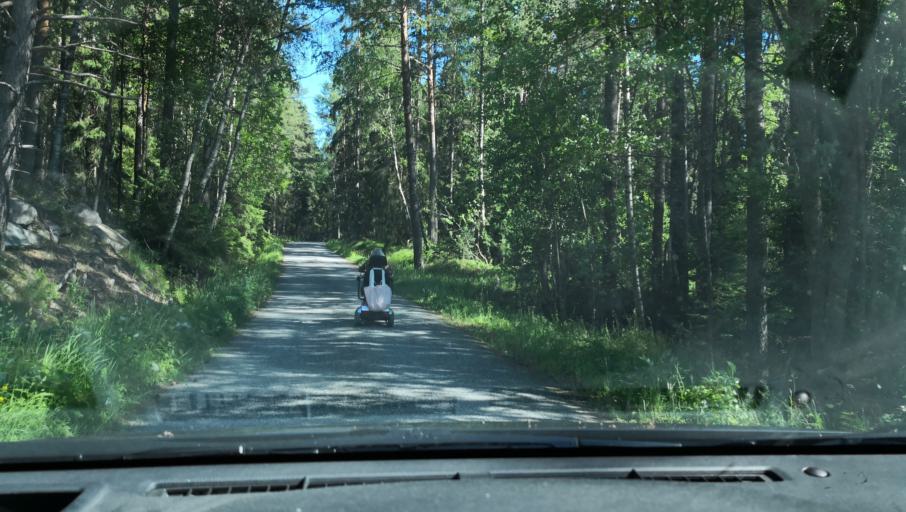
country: SE
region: Soedermanland
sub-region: Eskilstuna Kommun
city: Eskilstuna
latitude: 59.3412
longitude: 16.5633
